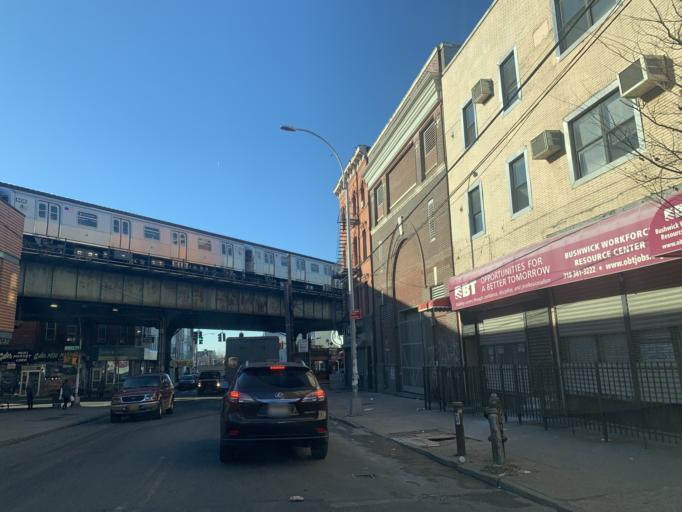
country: US
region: New York
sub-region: Kings County
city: East New York
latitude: 40.6998
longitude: -73.9119
